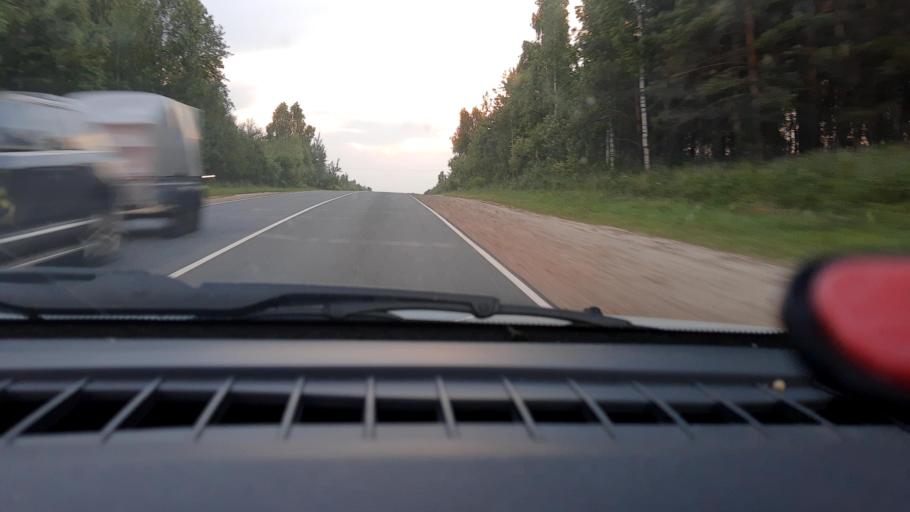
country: RU
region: Nizjnij Novgorod
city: Arzamas
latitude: 55.3904
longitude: 43.9172
